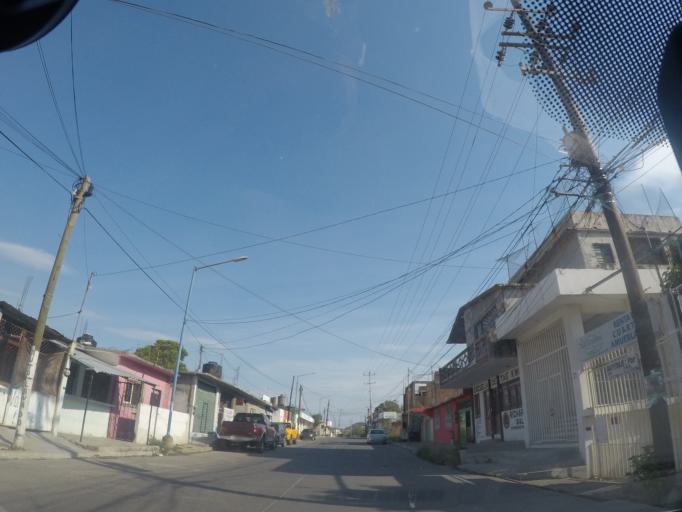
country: MX
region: Oaxaca
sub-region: Salina Cruz
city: Salina Cruz
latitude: 16.1954
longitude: -95.2025
